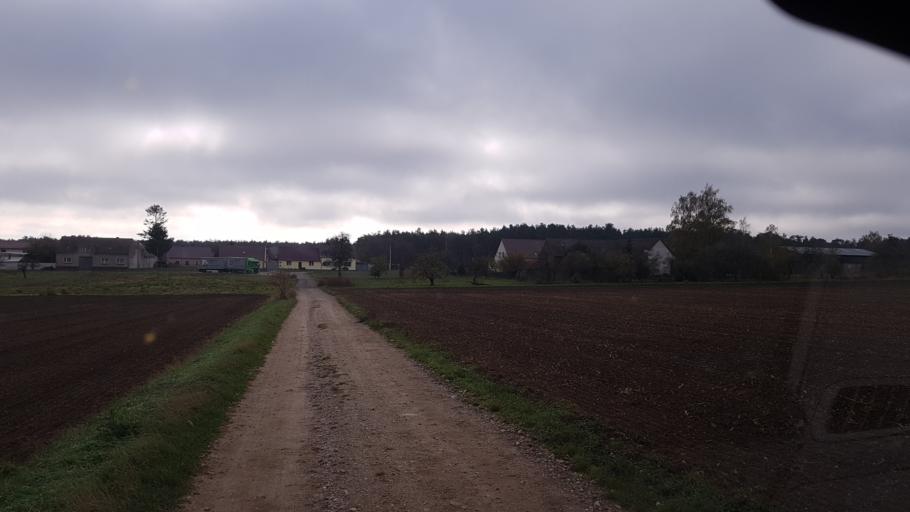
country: DE
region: Brandenburg
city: Schonborn
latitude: 51.6690
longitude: 13.4678
